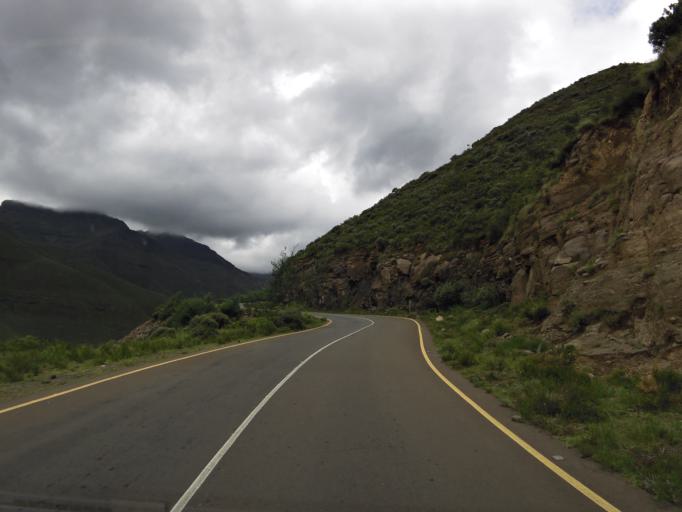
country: LS
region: Butha-Buthe
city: Butha-Buthe
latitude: -29.0547
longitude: 28.3490
